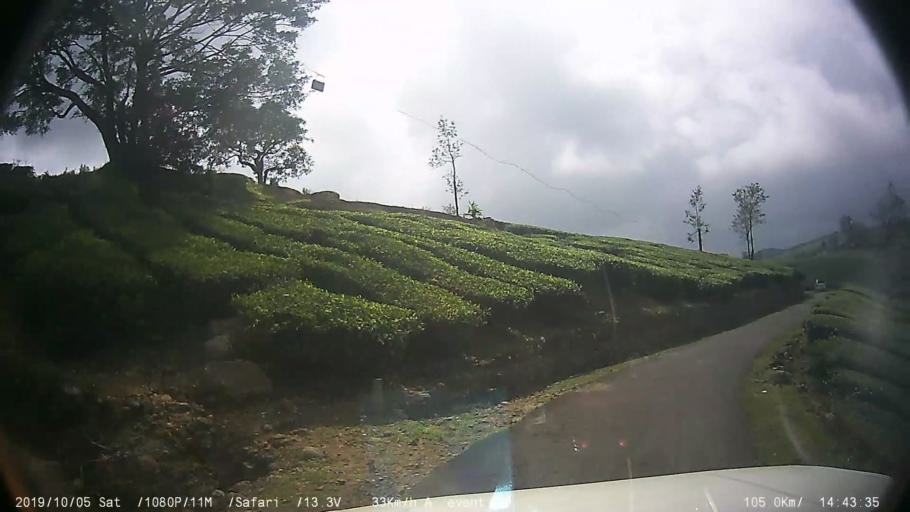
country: IN
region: Kerala
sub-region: Kottayam
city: Erattupetta
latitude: 9.6197
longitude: 76.9478
